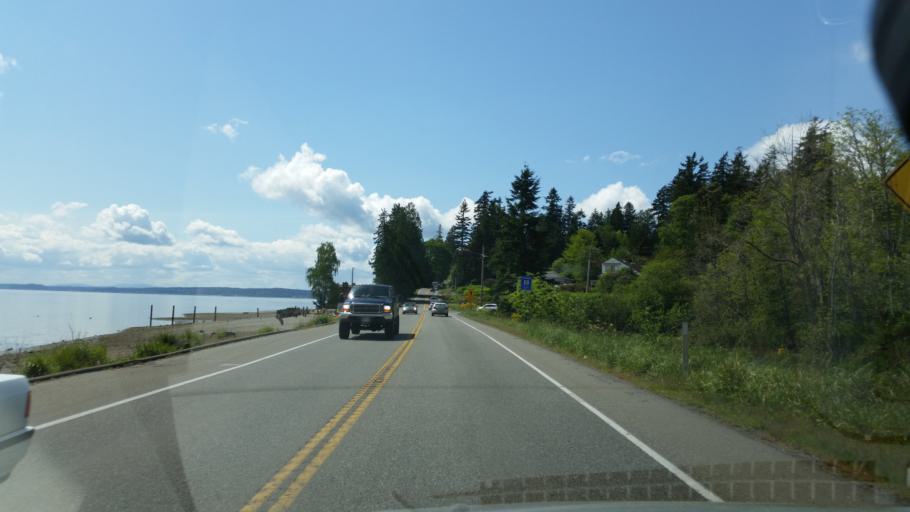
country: US
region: Washington
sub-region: Pierce County
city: Wauna
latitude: 47.3801
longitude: -122.6402
